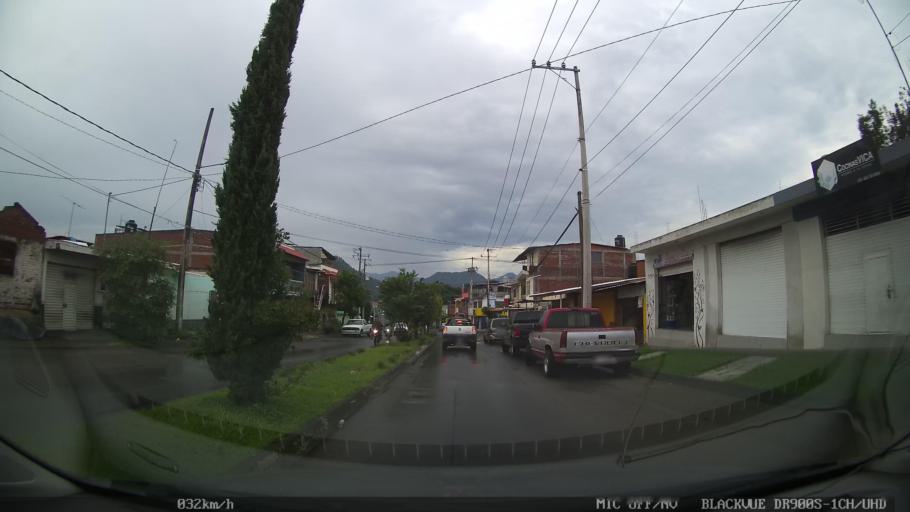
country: MX
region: Michoacan
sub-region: Uruapan
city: Santa Rosa (Santa Barbara)
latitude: 19.3886
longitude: -102.0534
